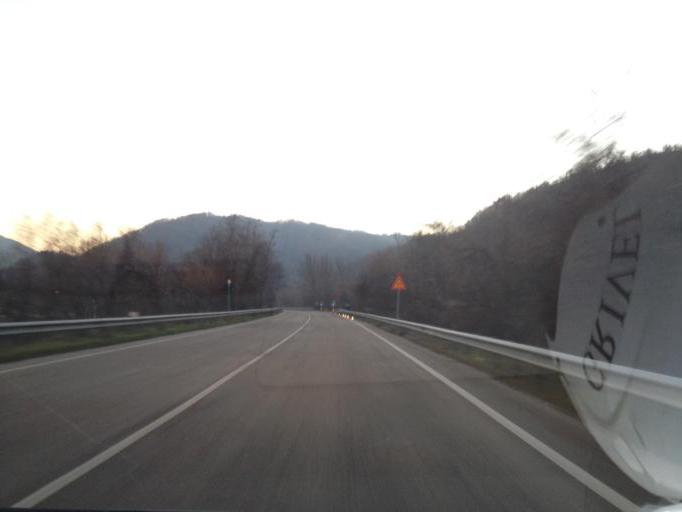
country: IT
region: The Marches
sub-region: Provincia di Ascoli Piceno
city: Arquata del Tronto
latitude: 42.7428
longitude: 13.2659
